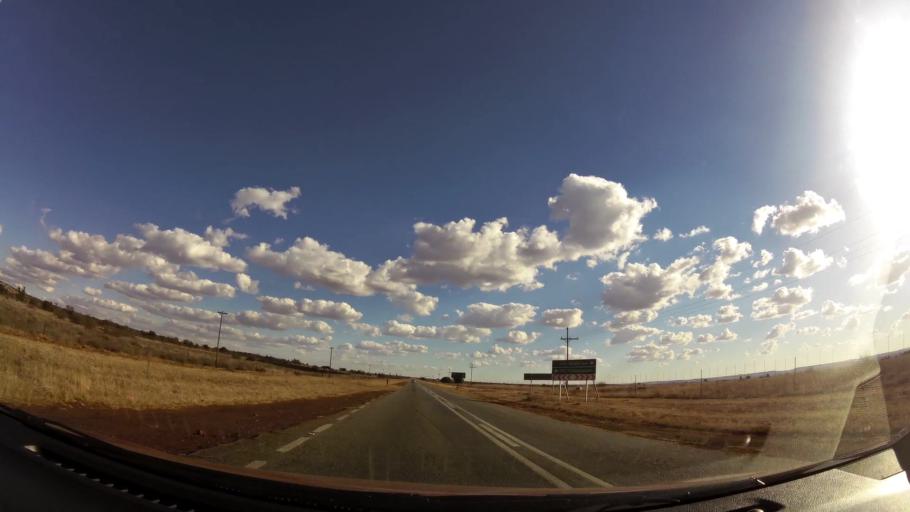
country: ZA
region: Gauteng
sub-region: West Rand District Municipality
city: Carletonville
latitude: -26.4139
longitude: 27.2341
